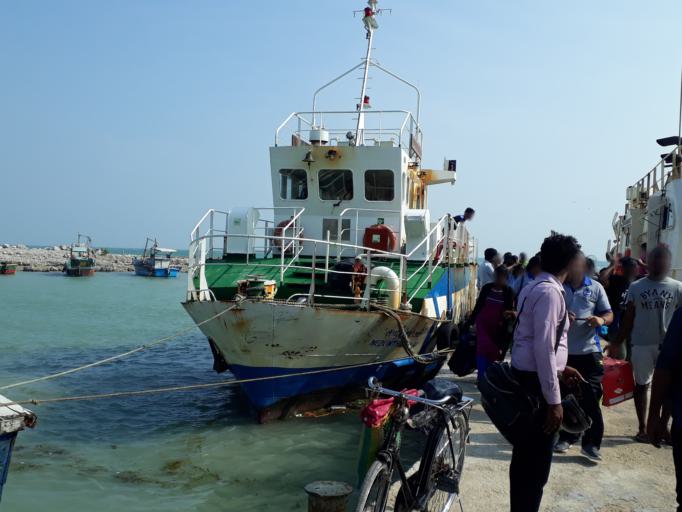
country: LK
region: Northern Province
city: Jaffna
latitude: 9.5281
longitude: 79.7169
